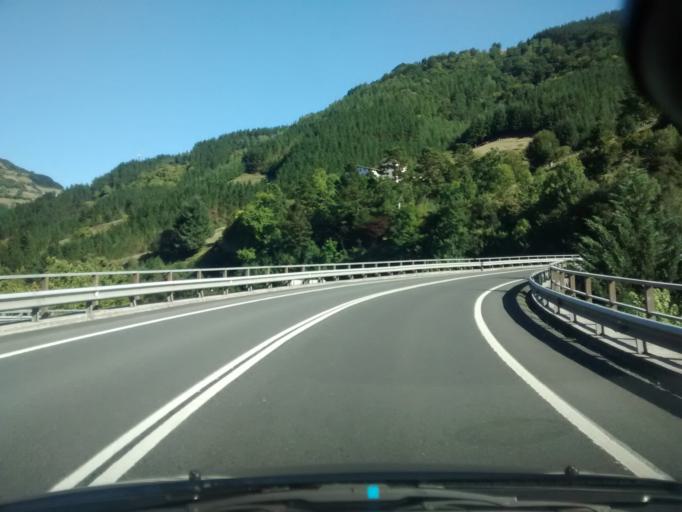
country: ES
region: Basque Country
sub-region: Provincia de Guipuzcoa
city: Eibar
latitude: 43.1910
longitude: -2.4479
